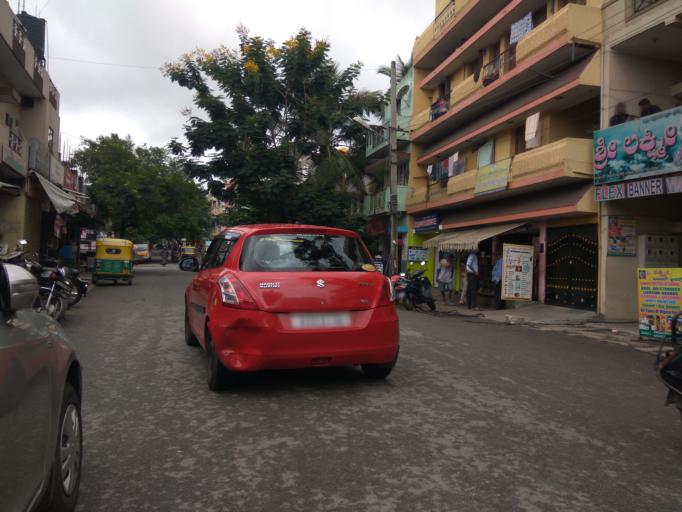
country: IN
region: Karnataka
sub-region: Bangalore Urban
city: Bangalore
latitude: 12.9794
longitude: 77.5392
